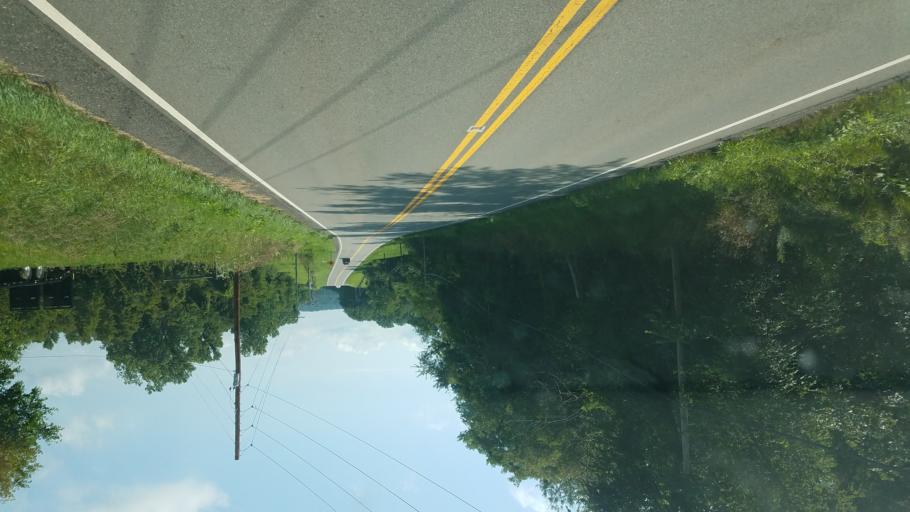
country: US
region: Ohio
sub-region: Licking County
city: Granville
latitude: 40.1371
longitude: -82.5192
